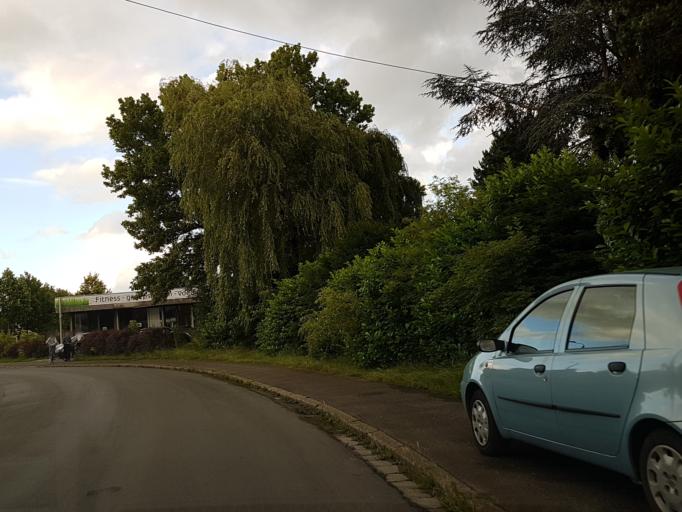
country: BE
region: Flanders
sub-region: Provincie Vlaams-Brabant
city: Opwijk
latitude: 50.9733
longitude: 4.1938
